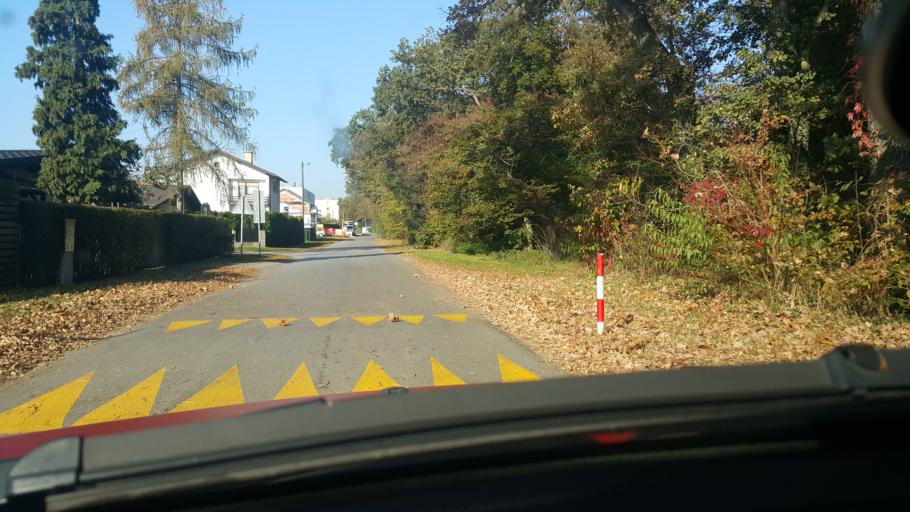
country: SI
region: Maribor
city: Maribor
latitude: 46.5365
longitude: 15.6664
